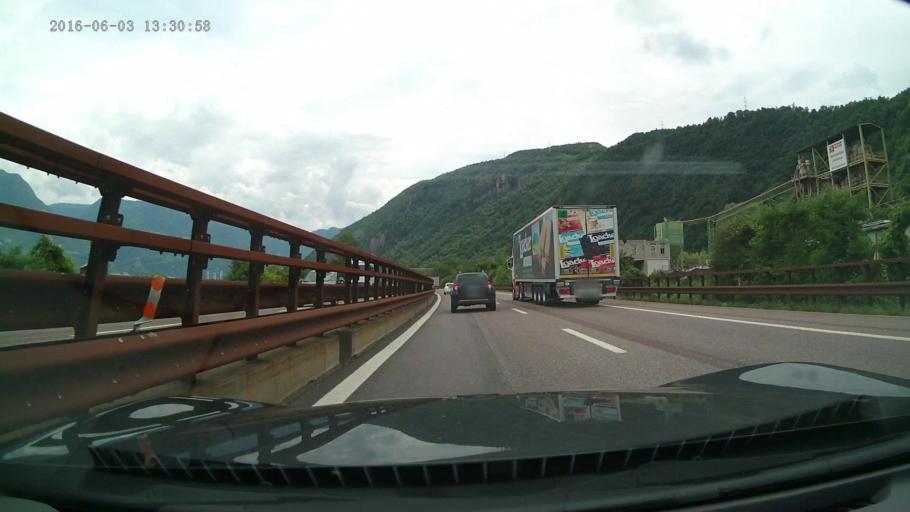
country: IT
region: Trentino-Alto Adige
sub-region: Bolzano
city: Cornaiano
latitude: 46.4582
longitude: 11.3039
